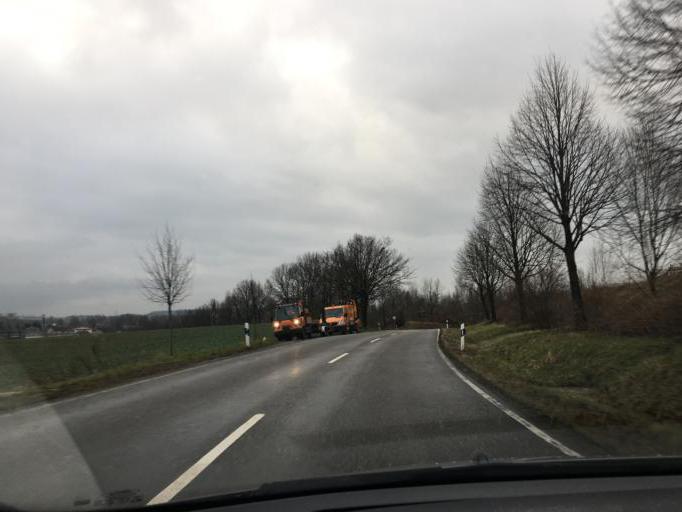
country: DE
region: Thuringia
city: Ziegelheim
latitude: 50.8982
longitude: 12.5356
